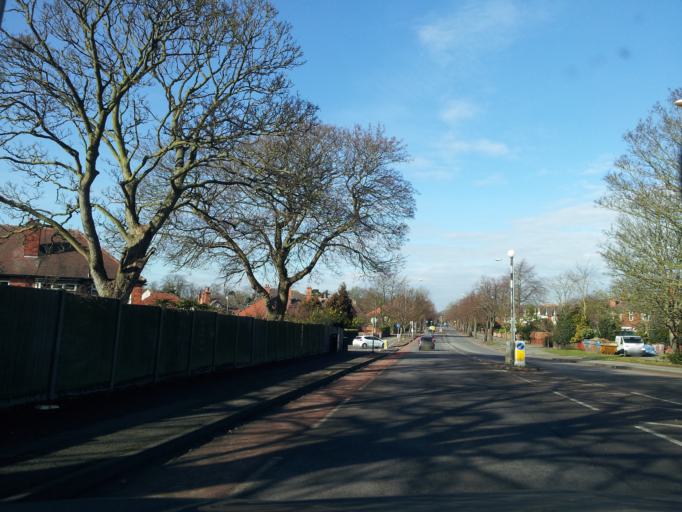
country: GB
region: England
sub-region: Nottinghamshire
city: Newark on Trent
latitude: 53.0670
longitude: -0.7947
